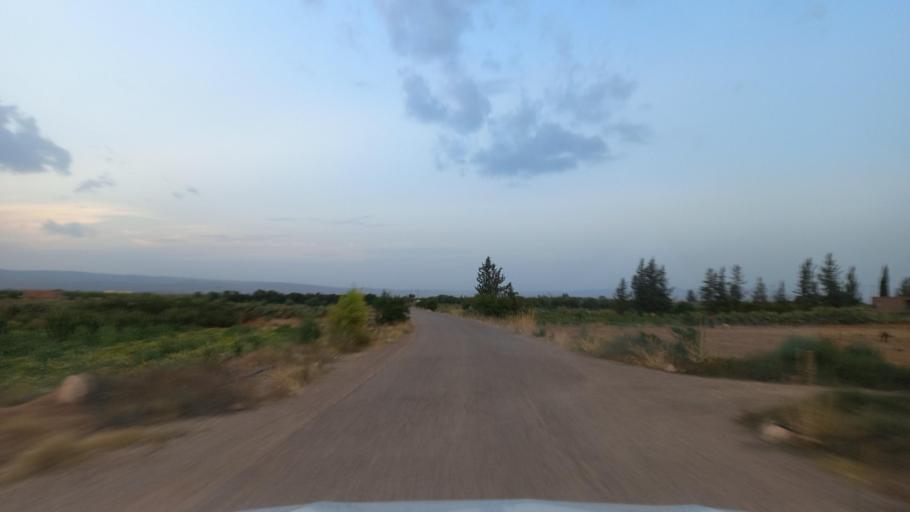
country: TN
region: Al Qasrayn
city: Kasserine
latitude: 35.2706
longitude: 9.0465
